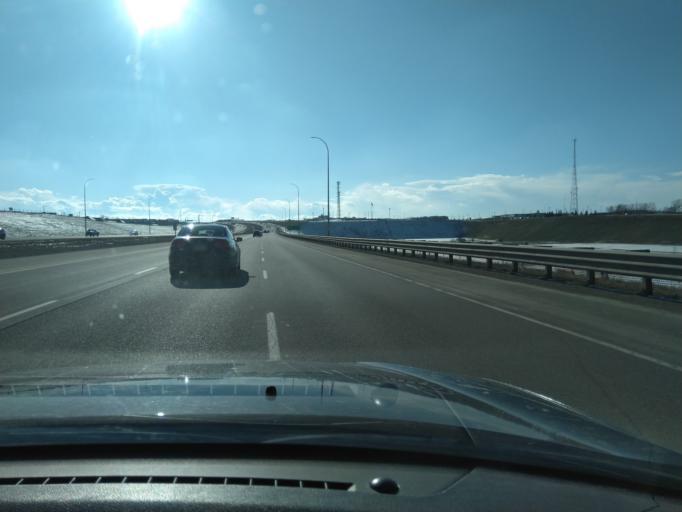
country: CA
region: Alberta
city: Calgary
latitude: 51.1515
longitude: -114.1769
